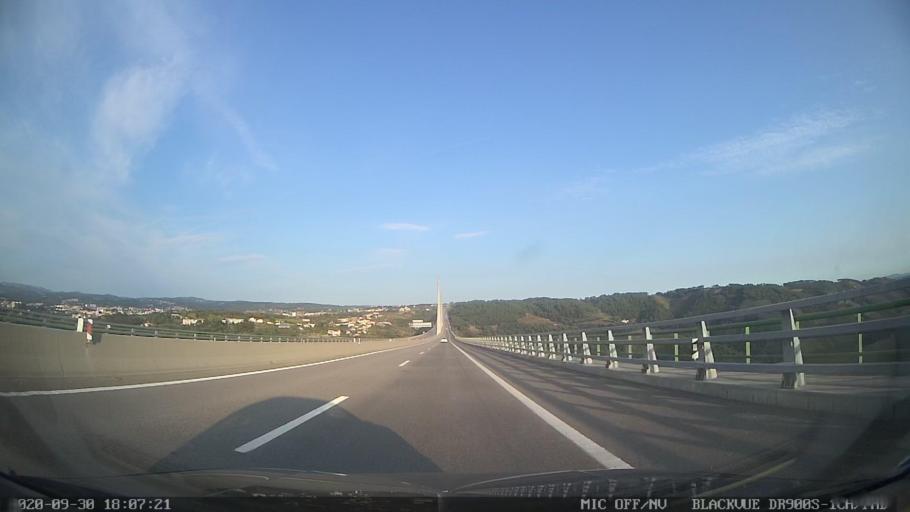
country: PT
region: Vila Real
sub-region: Vila Real
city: Vila Real
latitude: 41.2775
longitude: -7.7582
